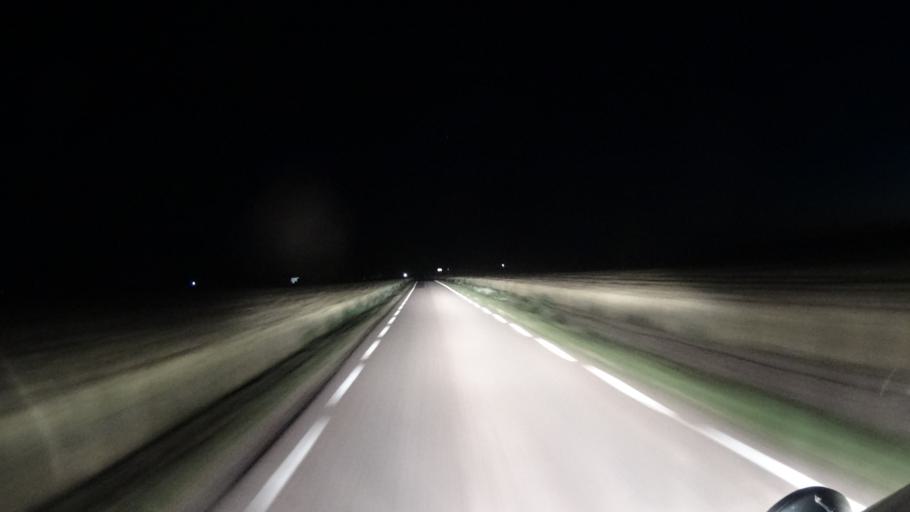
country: SE
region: OEstergoetland
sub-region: Vadstena Kommun
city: Herrestad
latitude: 58.3233
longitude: 14.8324
